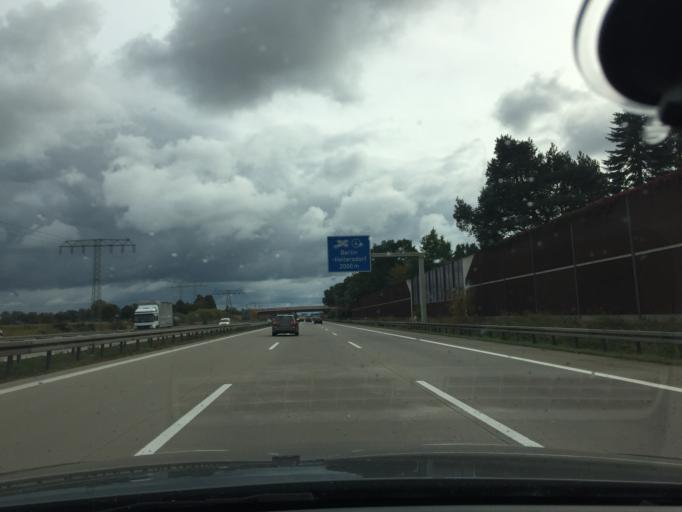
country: DE
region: Brandenburg
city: Neuenhagen
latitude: 52.5185
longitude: 13.7235
